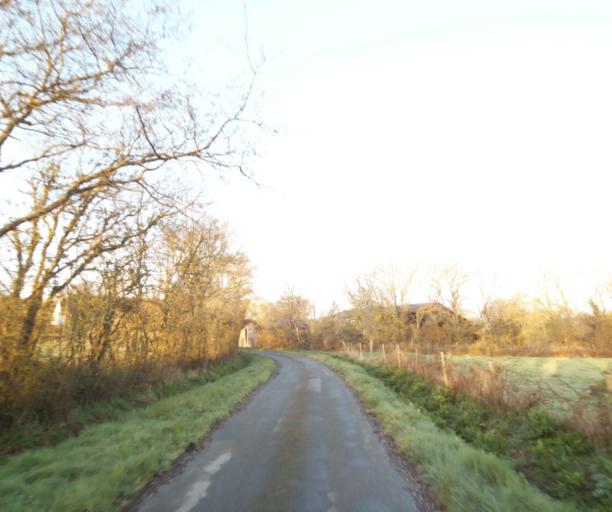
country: FR
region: Pays de la Loire
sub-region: Departement de la Loire-Atlantique
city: Bouvron
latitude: 47.4363
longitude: -1.8999
